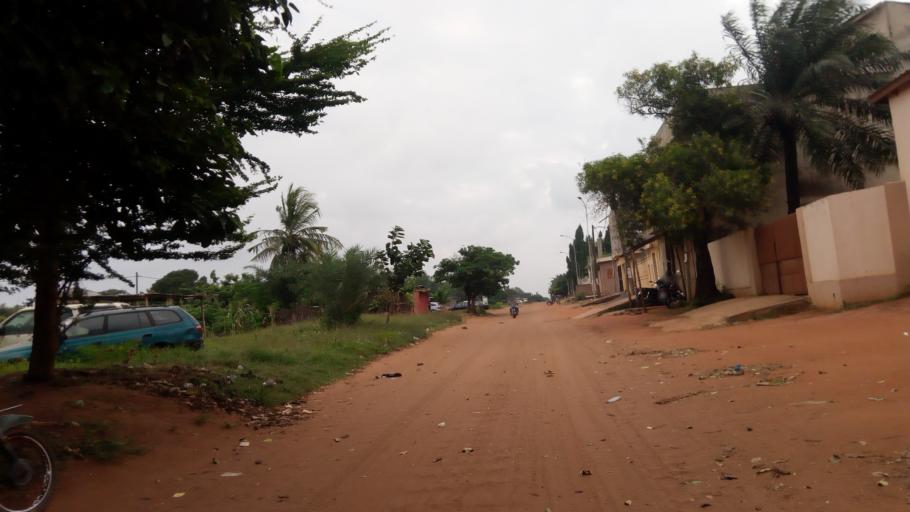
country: TG
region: Maritime
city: Lome
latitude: 6.1716
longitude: 1.1971
